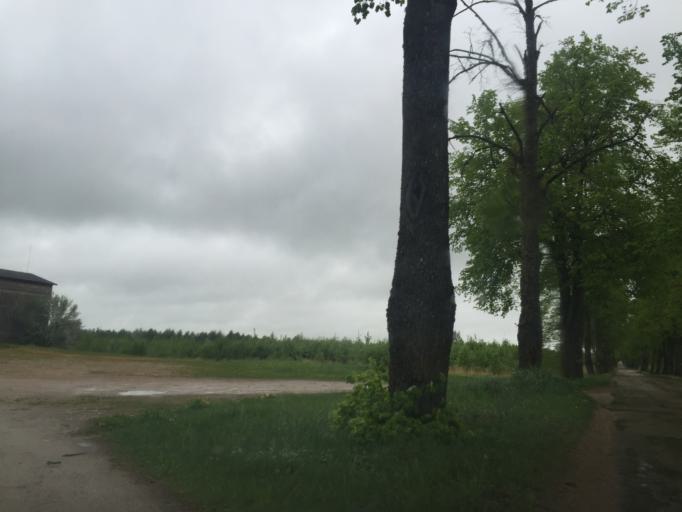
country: LV
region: Ogre
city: Jumprava
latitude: 56.6440
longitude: 24.9195
